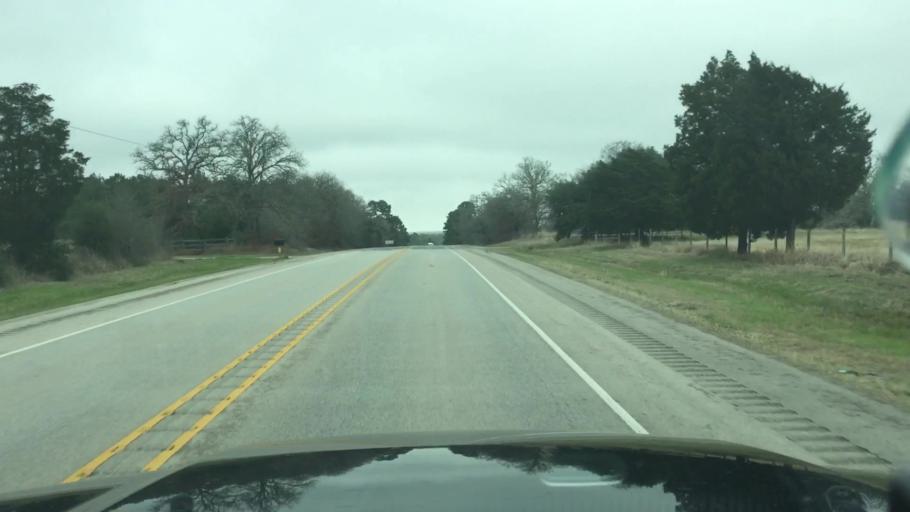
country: US
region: Texas
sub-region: Lee County
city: Giddings
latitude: 30.0763
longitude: -96.9170
